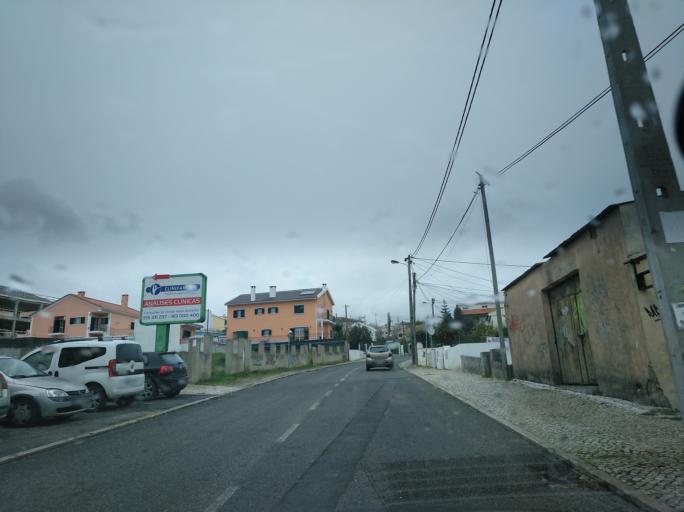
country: PT
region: Lisbon
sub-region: Odivelas
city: Famoes
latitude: 38.7923
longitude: -9.2109
